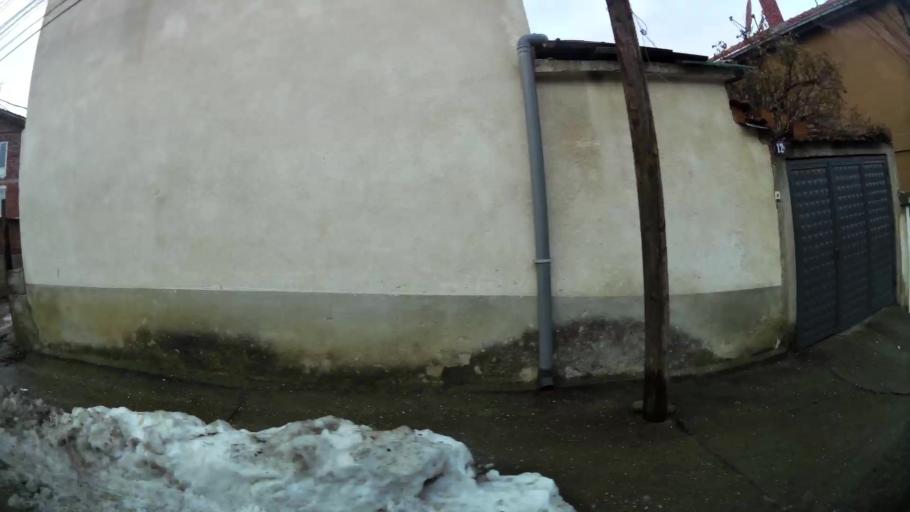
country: XK
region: Pristina
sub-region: Komuna e Prishtines
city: Pristina
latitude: 42.6636
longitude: 21.1720
